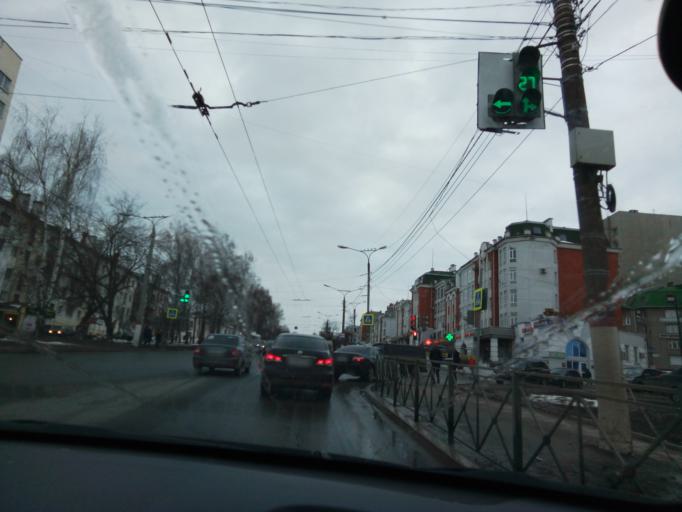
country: RU
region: Chuvashia
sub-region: Cheboksarskiy Rayon
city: Cheboksary
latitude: 56.1464
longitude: 47.2333
